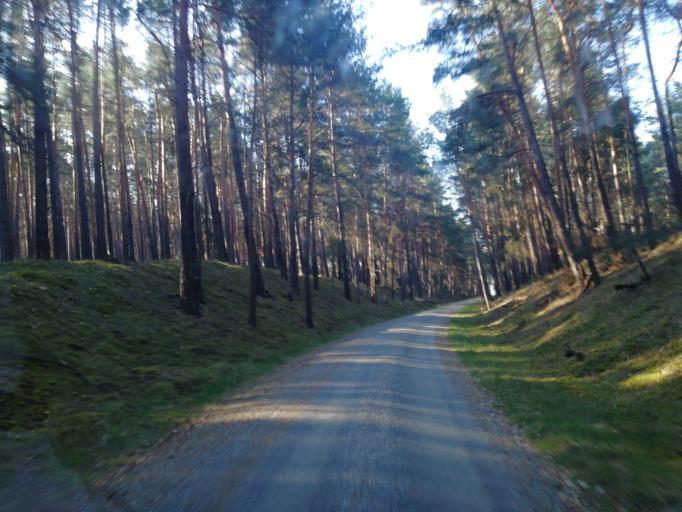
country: DE
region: Brandenburg
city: Drahnsdorf
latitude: 51.8928
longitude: 13.5277
